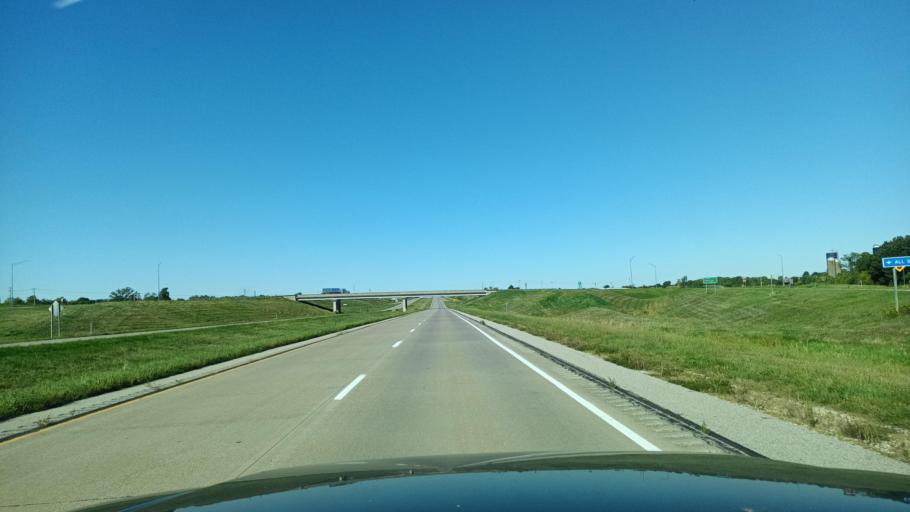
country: US
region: Iowa
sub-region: Lee County
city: Fort Madison
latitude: 40.6707
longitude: -91.3234
